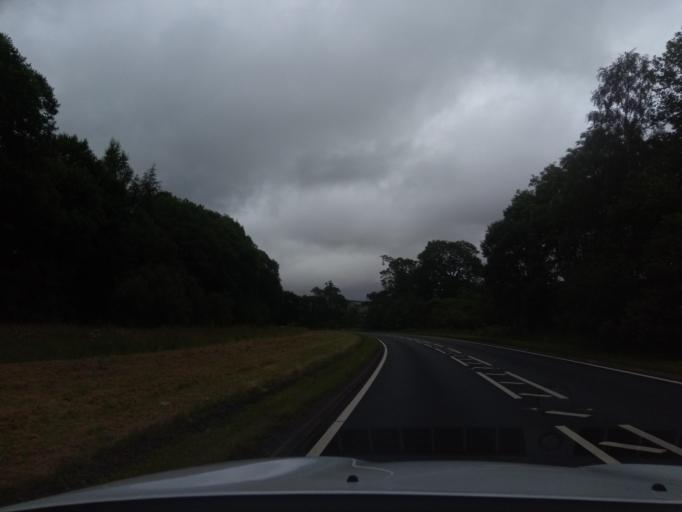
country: GB
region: Scotland
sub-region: The Scottish Borders
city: Earlston
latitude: 55.6218
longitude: -2.6781
